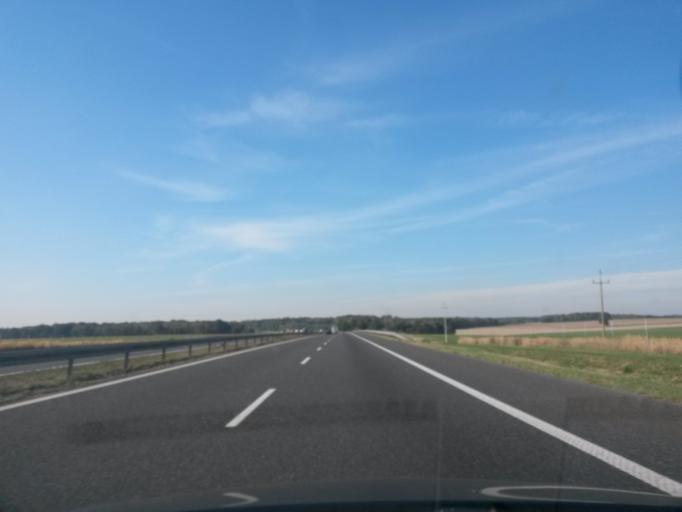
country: PL
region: Opole Voivodeship
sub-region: Powiat strzelecki
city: Ujazd
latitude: 50.4187
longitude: 18.4008
